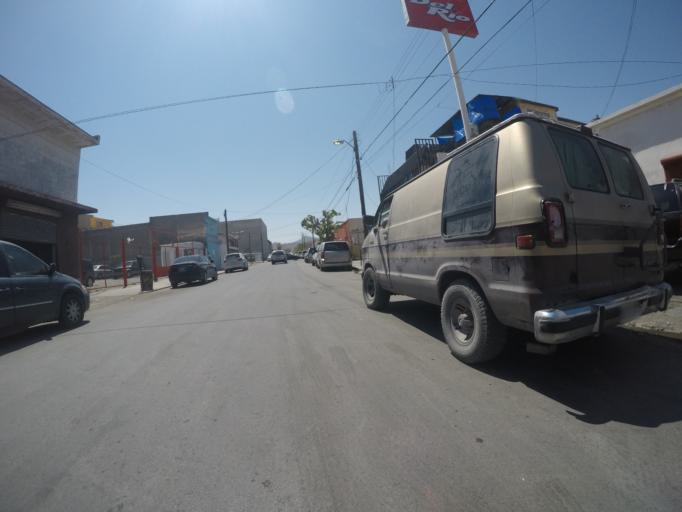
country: MX
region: Chihuahua
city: Ciudad Juarez
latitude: 31.7357
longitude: -106.4890
